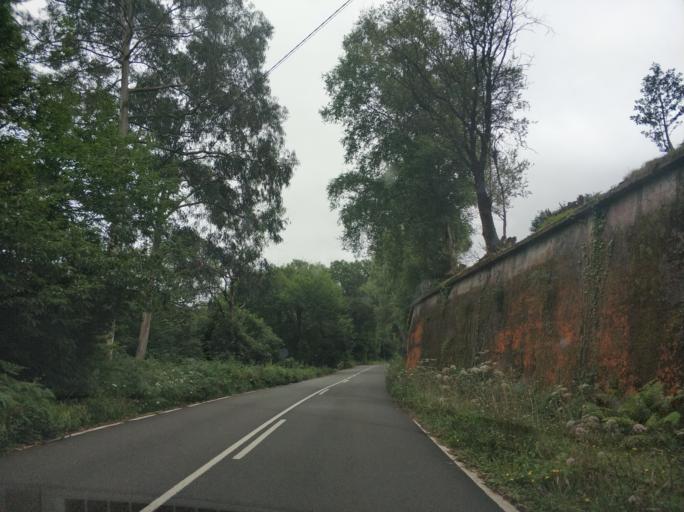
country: ES
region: Asturias
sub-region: Province of Asturias
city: Cudillero
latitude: 43.5579
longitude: -6.2894
